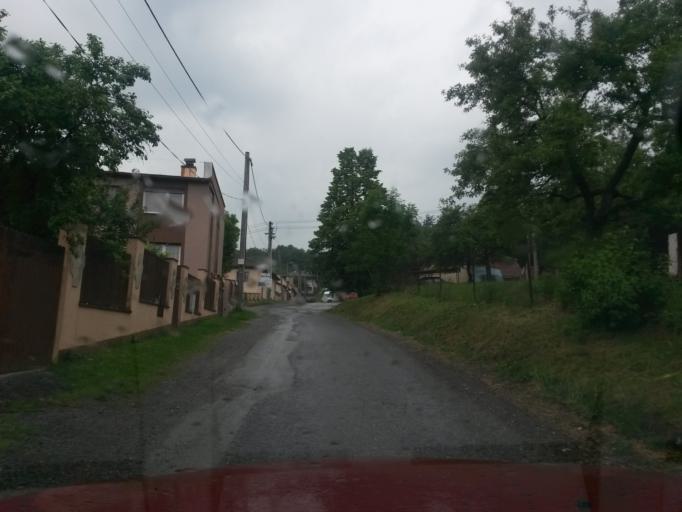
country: SK
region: Kosicky
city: Kosice
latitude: 48.7072
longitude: 21.1795
